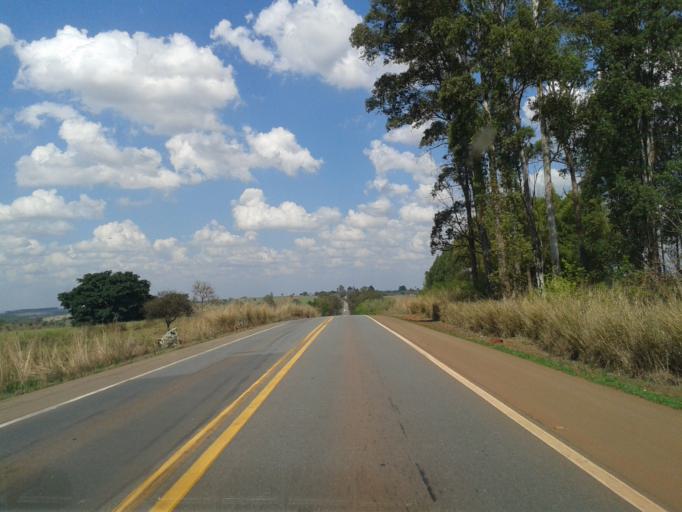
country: BR
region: Minas Gerais
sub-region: Luz
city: Luz
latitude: -19.7766
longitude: -45.7491
